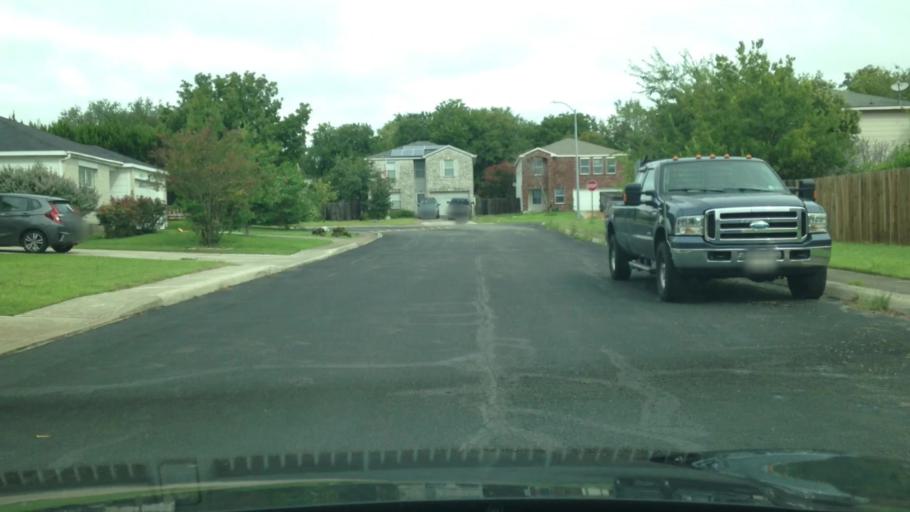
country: US
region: Texas
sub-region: Bexar County
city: Windcrest
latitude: 29.5697
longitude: -98.4166
